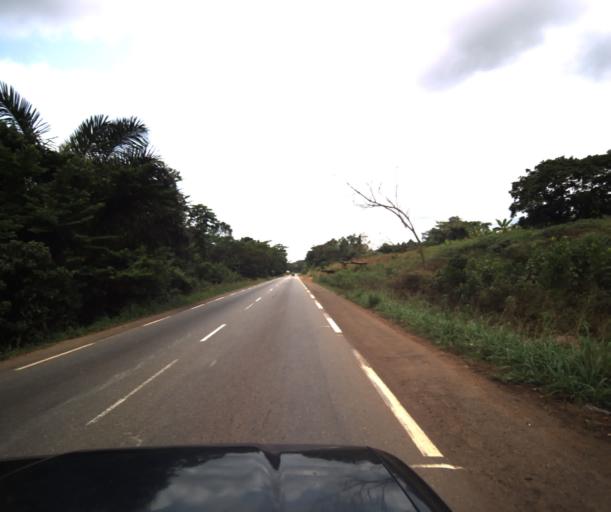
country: CM
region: Centre
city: Eseka
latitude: 3.8437
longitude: 10.9767
